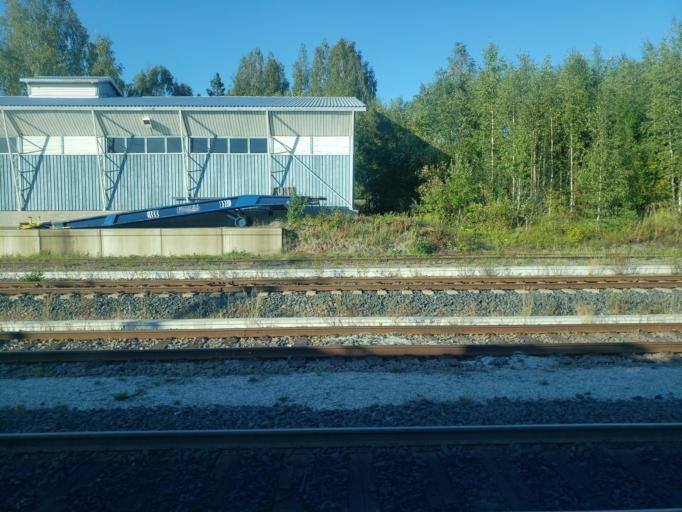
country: FI
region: South Karelia
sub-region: Lappeenranta
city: Lappeenranta
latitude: 60.8662
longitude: 28.2938
